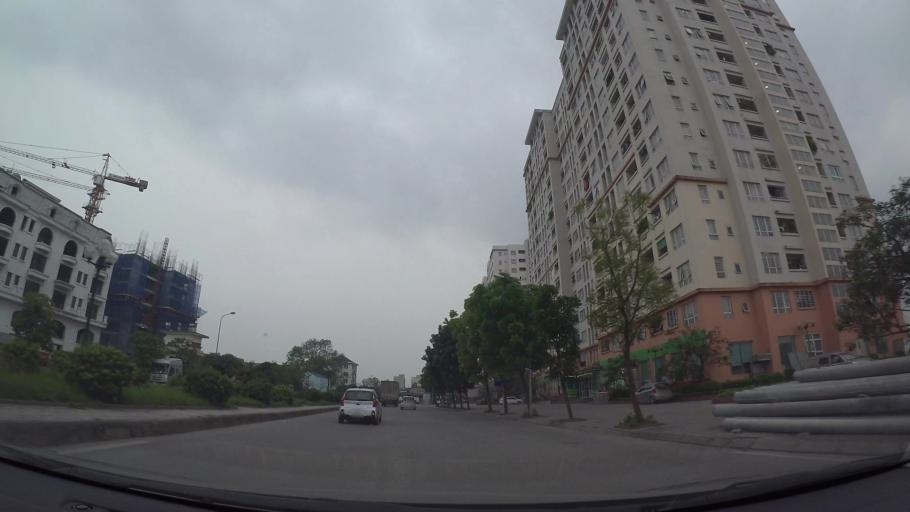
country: VN
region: Ha Noi
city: Trau Quy
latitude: 21.0402
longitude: 105.9130
